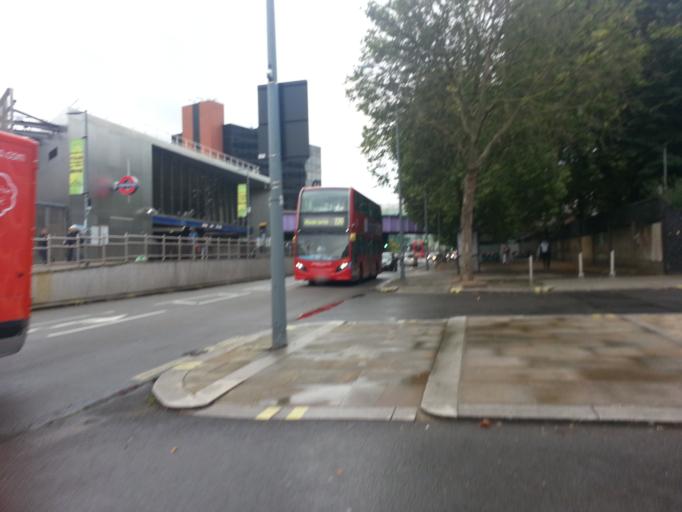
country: GB
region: England
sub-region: Greater London
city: Hammersmith
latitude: 51.5104
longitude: -0.2247
